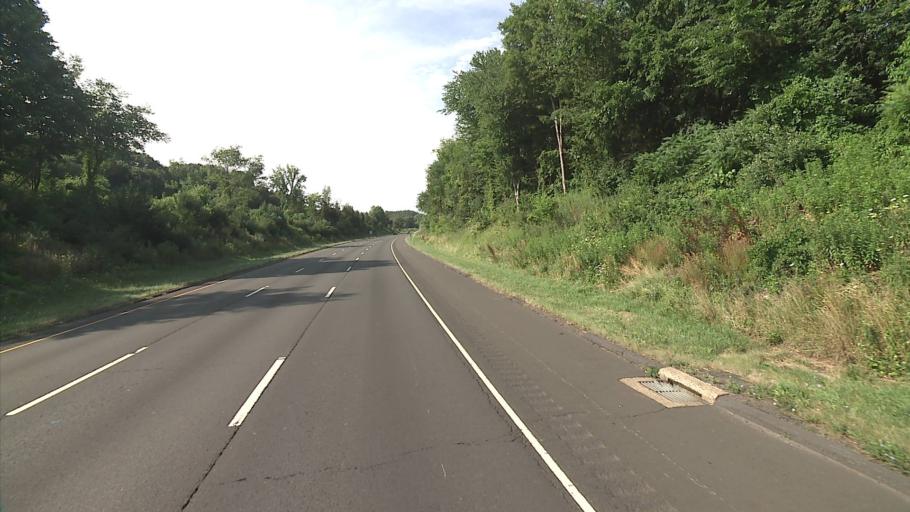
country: US
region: Connecticut
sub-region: Middlesex County
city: Cromwell
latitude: 41.5894
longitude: -72.7109
